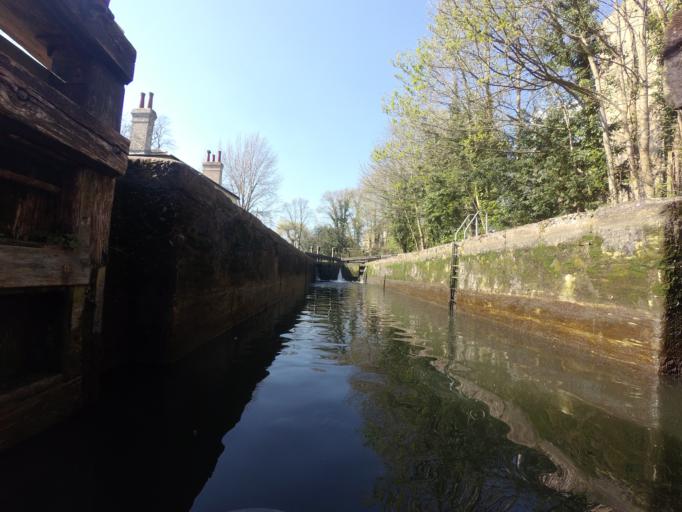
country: GB
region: England
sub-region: Hertfordshire
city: Kings Langley
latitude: 51.7296
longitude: -0.4538
